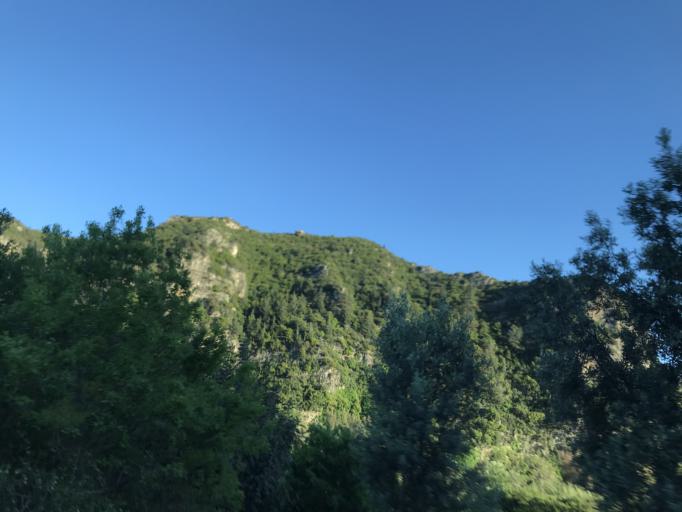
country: TR
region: Hatay
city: Buyukcat
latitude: 36.0772
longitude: 36.0351
